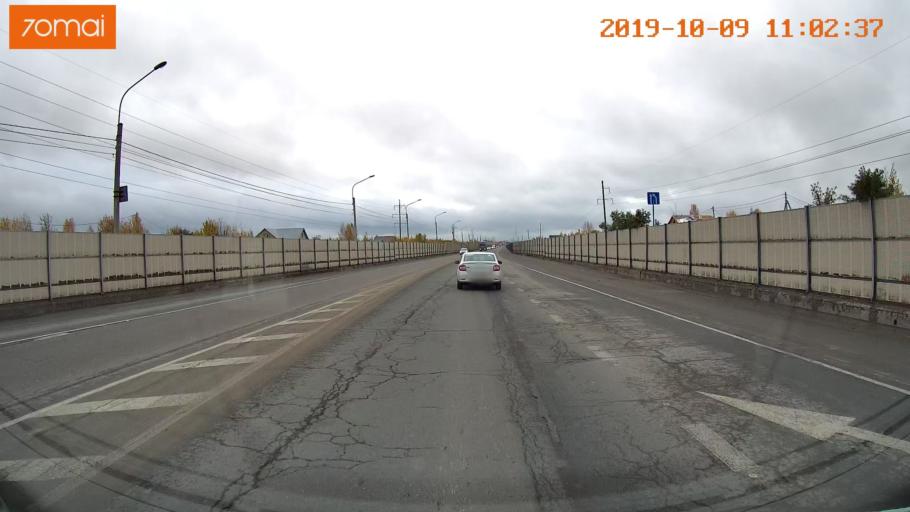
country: RU
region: Vologda
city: Vologda
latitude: 59.2294
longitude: 39.7745
